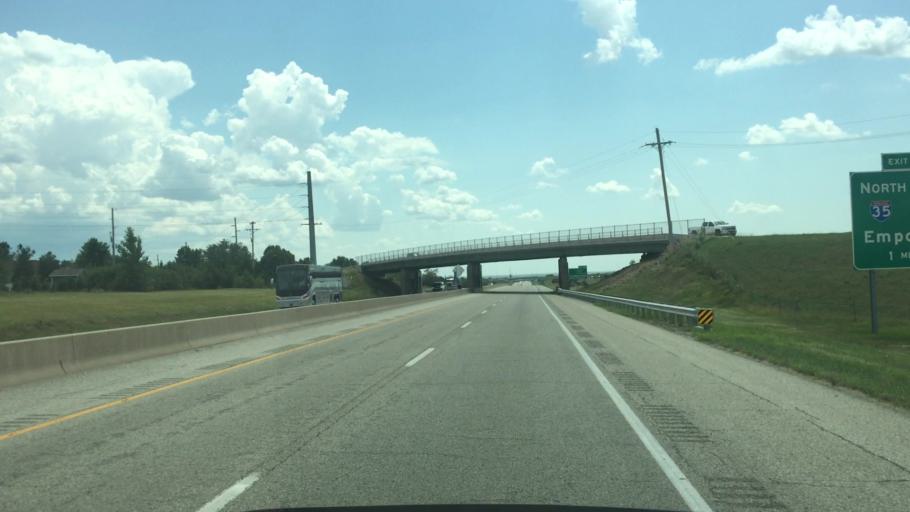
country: US
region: Kansas
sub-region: Lyon County
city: Emporia
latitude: 38.4321
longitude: -96.2255
